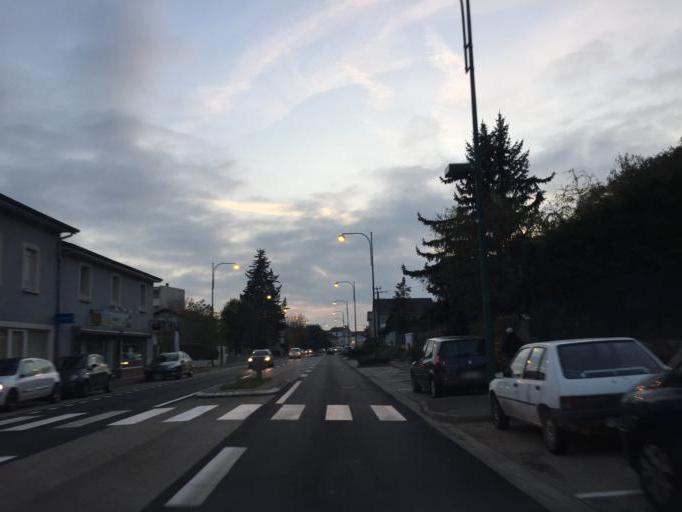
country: FR
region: Rhone-Alpes
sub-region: Departement de l'Ain
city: Beligneux
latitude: 45.8515
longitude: 5.1271
